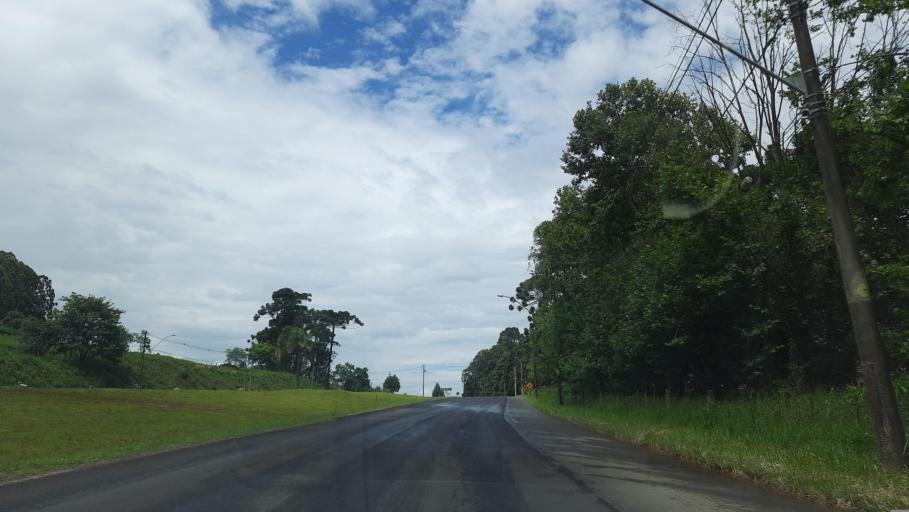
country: BR
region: Minas Gerais
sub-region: Pocos De Caldas
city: Pocos de Caldas
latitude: -21.7978
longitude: -46.6469
